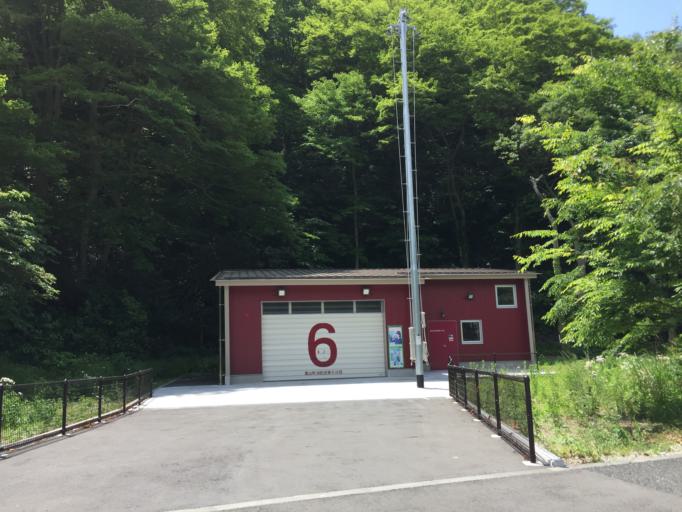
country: JP
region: Kanagawa
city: Hayama
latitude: 35.2828
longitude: 139.5816
